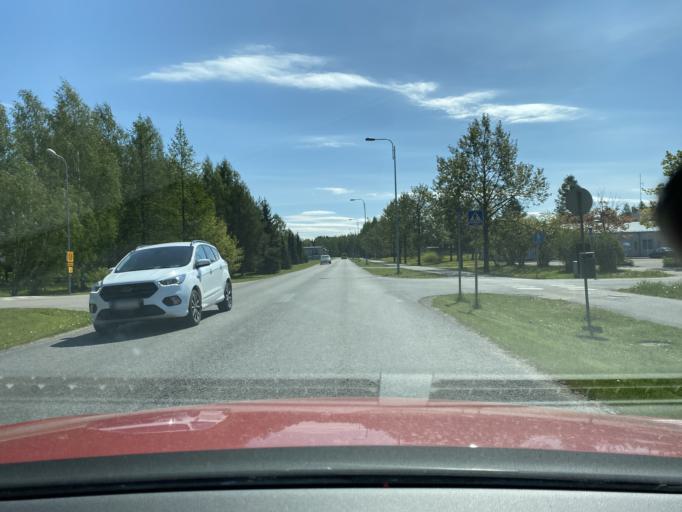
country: FI
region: Satakunta
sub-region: Rauma
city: Eura
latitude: 61.1259
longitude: 22.1488
